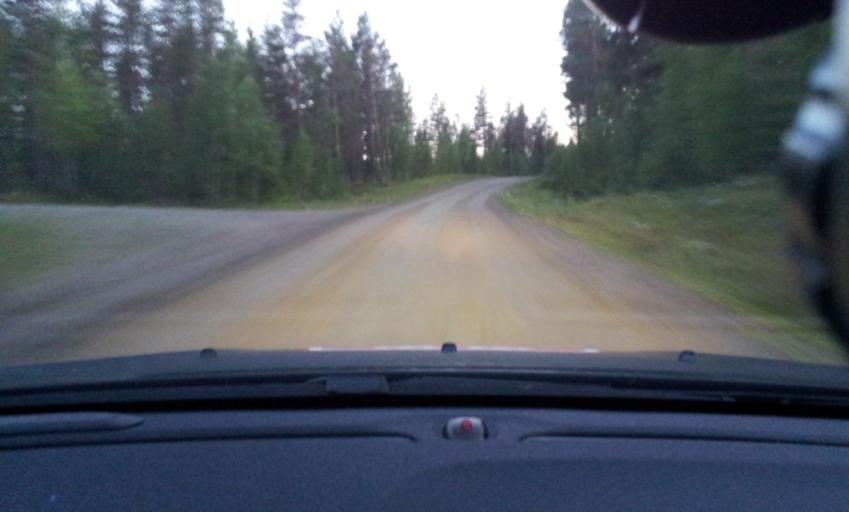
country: SE
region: Vaesternorrland
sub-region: Ange Kommun
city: Ange
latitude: 62.7679
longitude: 15.8579
